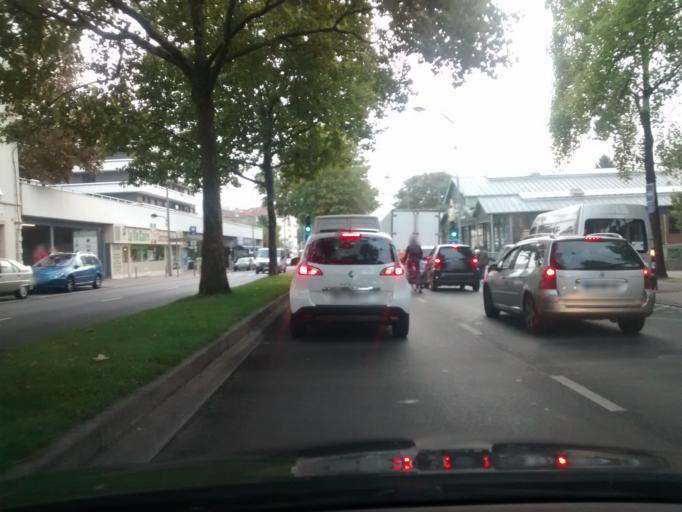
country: FR
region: Ile-de-France
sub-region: Departement des Hauts-de-Seine
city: Sevres
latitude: 48.8248
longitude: 2.2140
